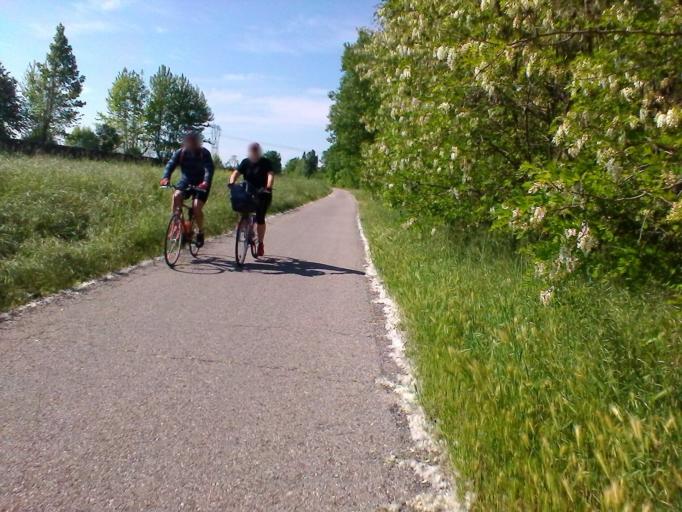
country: IT
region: Lombardy
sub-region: Provincia di Mantova
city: Roverbella
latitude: 45.2527
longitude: 10.7315
